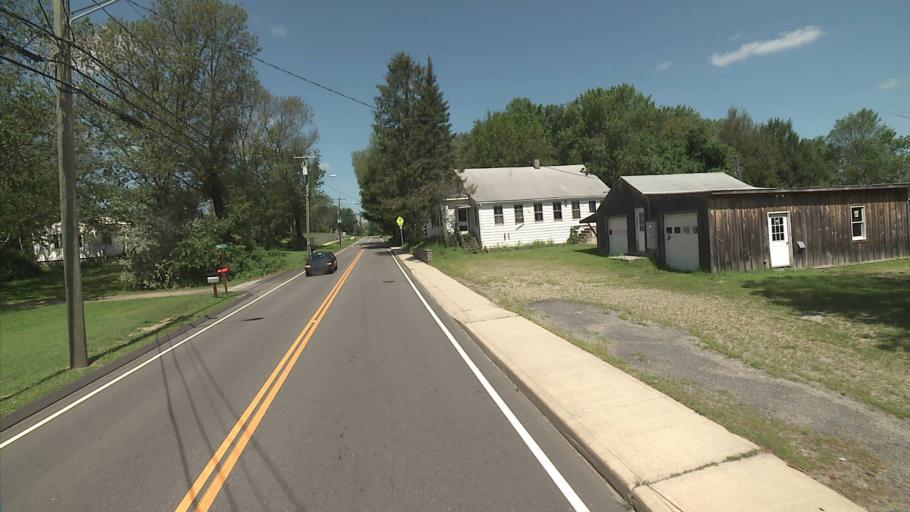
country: US
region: Connecticut
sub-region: Windham County
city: Plainfield Village
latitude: 41.6824
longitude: -71.9281
